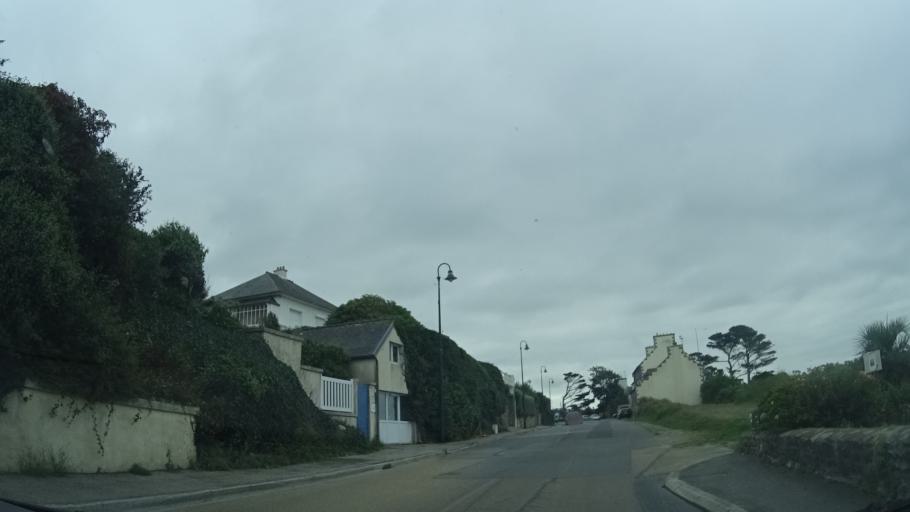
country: FR
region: Brittany
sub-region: Departement du Finistere
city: Lampaul-Plouarzel
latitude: 48.4743
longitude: -4.7501
